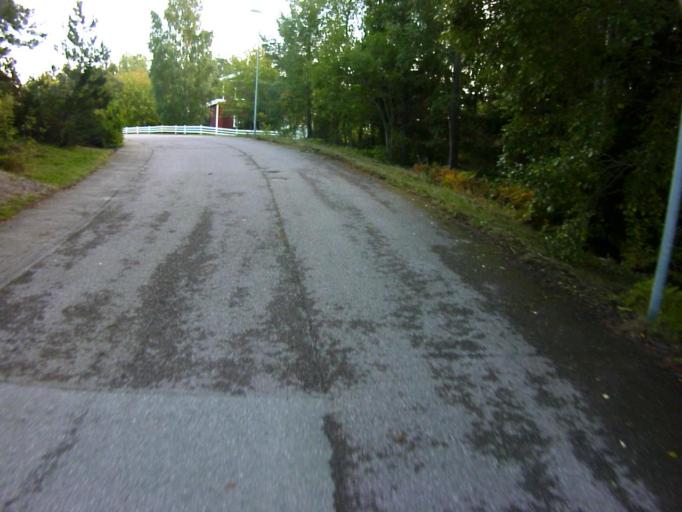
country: SE
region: Soedermanland
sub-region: Eskilstuna Kommun
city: Eskilstuna
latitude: 59.3863
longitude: 16.5449
